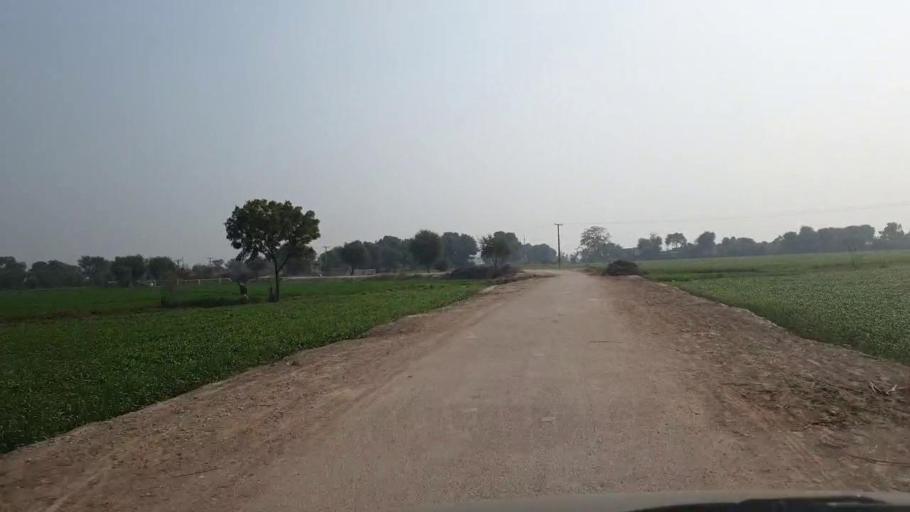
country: PK
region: Sindh
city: Bhit Shah
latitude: 25.8455
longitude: 68.4930
